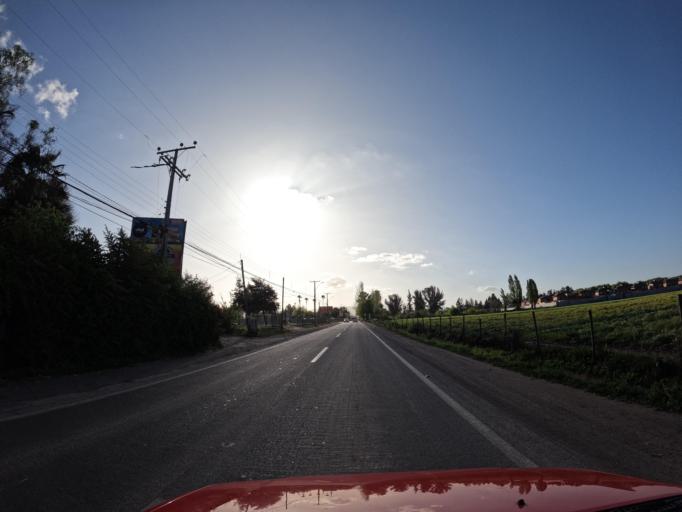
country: CL
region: O'Higgins
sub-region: Provincia de Colchagua
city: Santa Cruz
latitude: -34.6501
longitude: -71.3521
